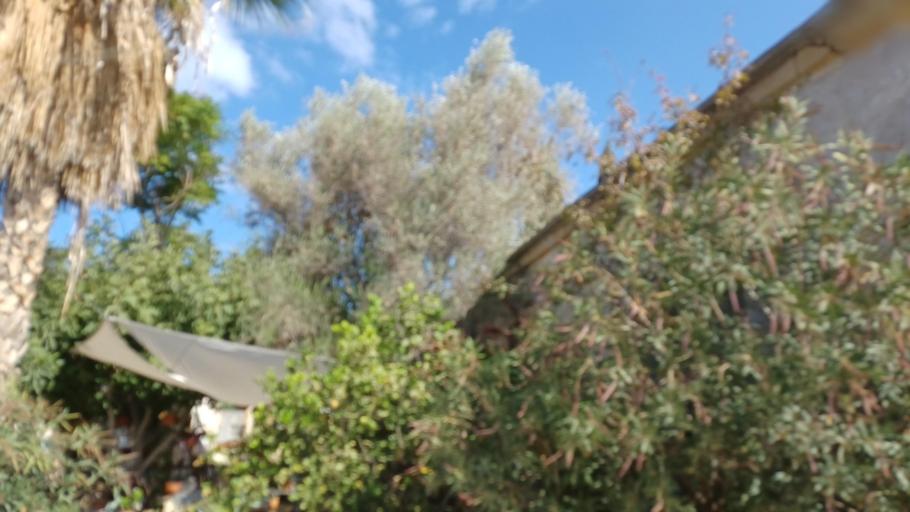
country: CY
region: Pafos
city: Polis
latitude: 35.0356
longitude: 32.4230
